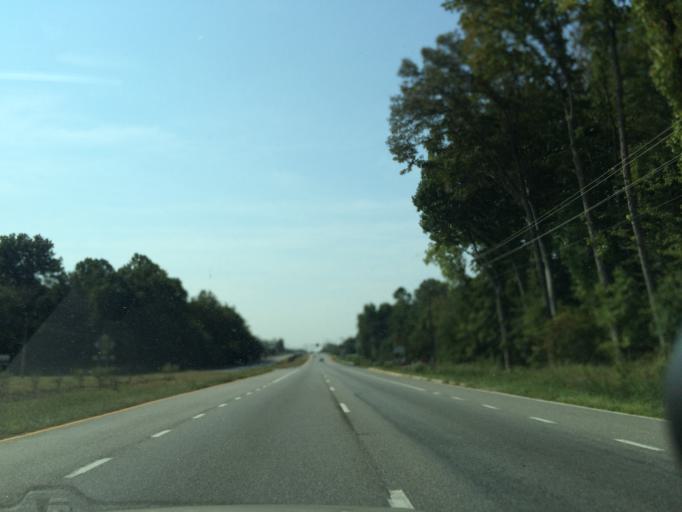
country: US
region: Maryland
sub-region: Charles County
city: La Plata
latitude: 38.5541
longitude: -76.9863
